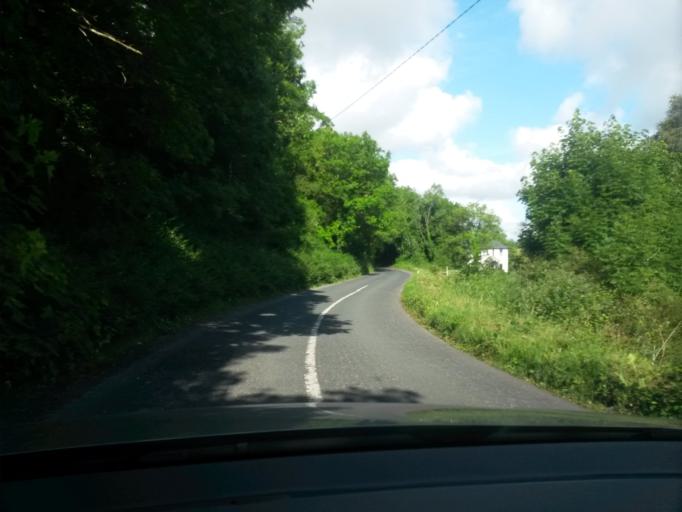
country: IE
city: Ballisodare
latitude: 54.2276
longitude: -8.4798
